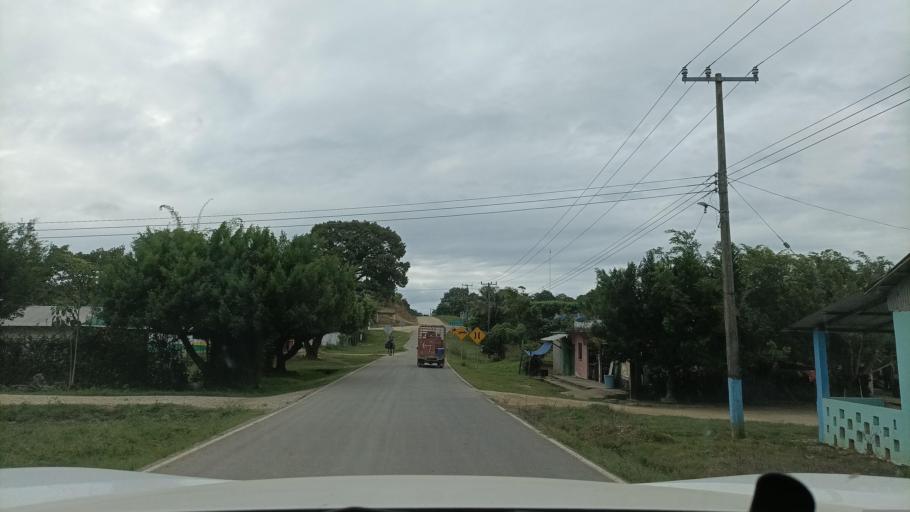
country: MX
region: Veracruz
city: Hidalgotitlan
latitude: 17.6591
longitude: -94.4038
